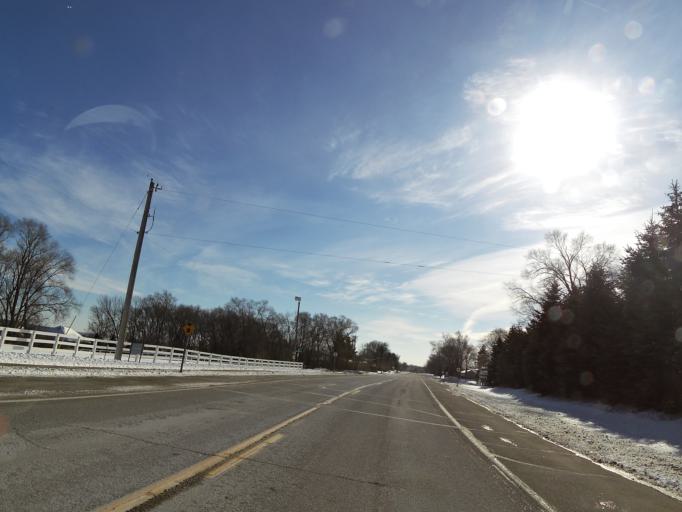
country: US
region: Minnesota
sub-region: Dakota County
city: Hastings
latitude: 44.7558
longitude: -92.8854
